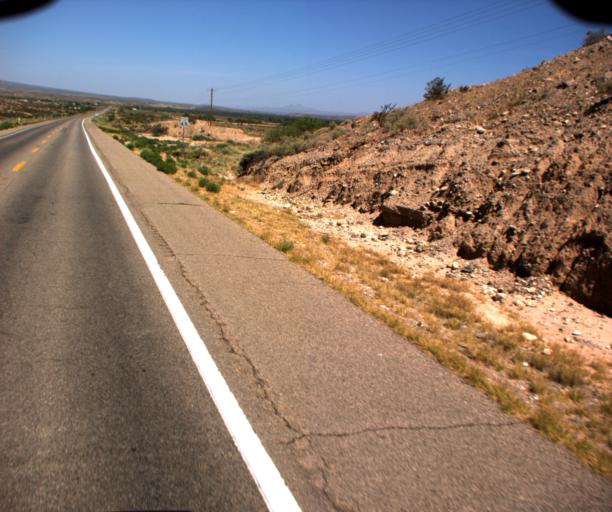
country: US
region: Arizona
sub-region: Graham County
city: Bylas
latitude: 33.0792
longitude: -110.0401
